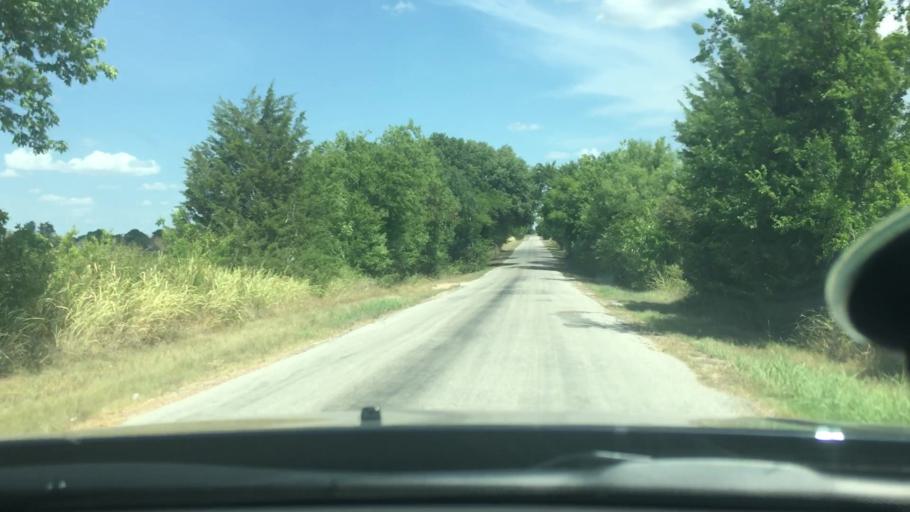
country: US
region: Oklahoma
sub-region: Love County
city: Marietta
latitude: 34.0028
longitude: -97.1935
